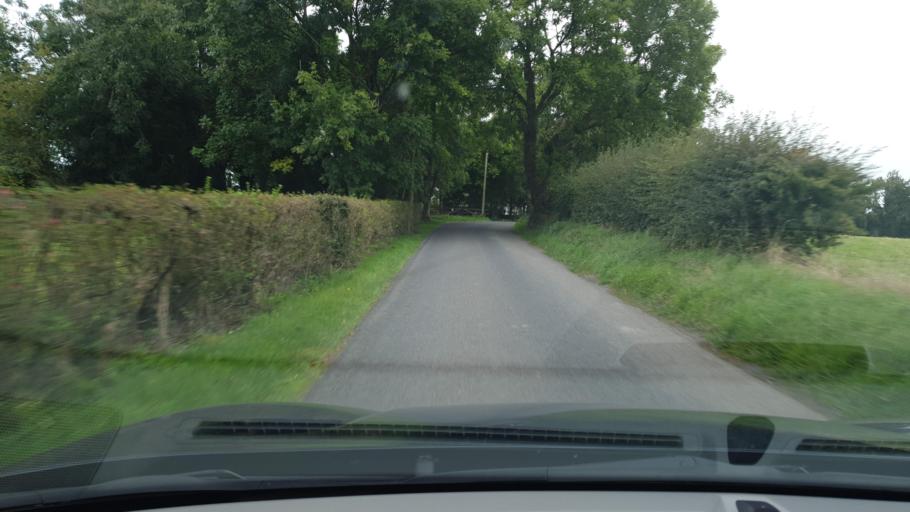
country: IE
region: Leinster
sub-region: An Mhi
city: Dunshaughlin
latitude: 53.5533
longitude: -6.5185
